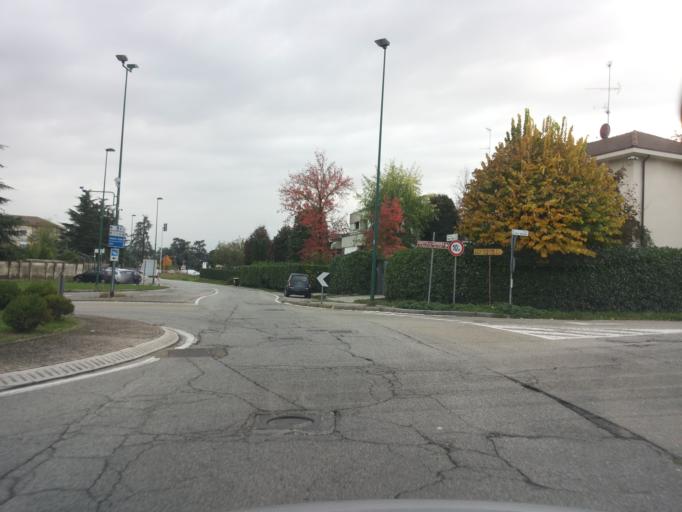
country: IT
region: Piedmont
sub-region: Provincia di Alessandria
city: Casale Monferrato
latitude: 45.1220
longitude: 8.4445
